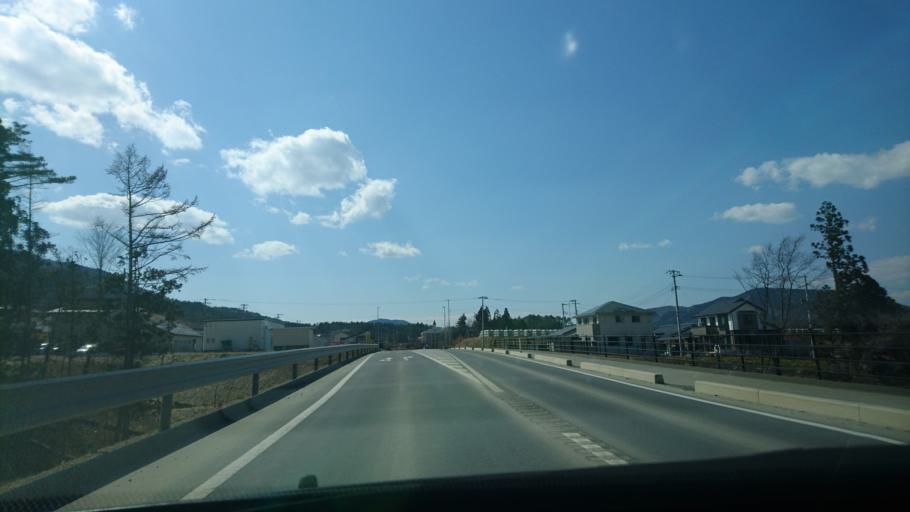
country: JP
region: Miyagi
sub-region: Oshika Gun
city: Onagawa Cho
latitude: 38.6383
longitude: 141.4448
